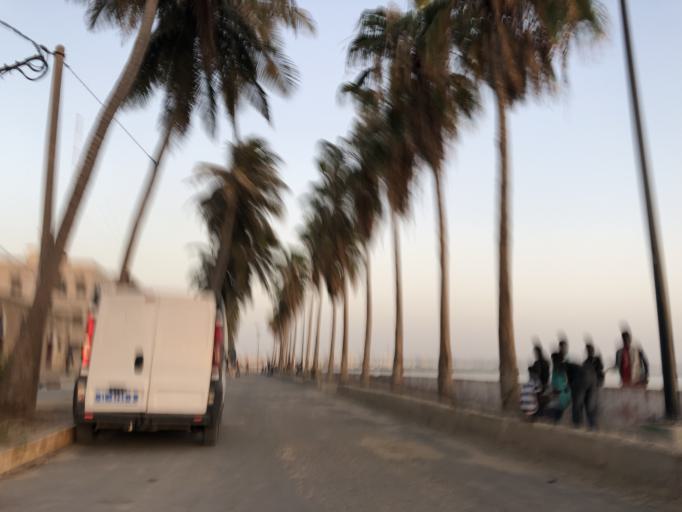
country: SN
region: Saint-Louis
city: Saint-Louis
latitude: 16.0189
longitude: -16.5065
